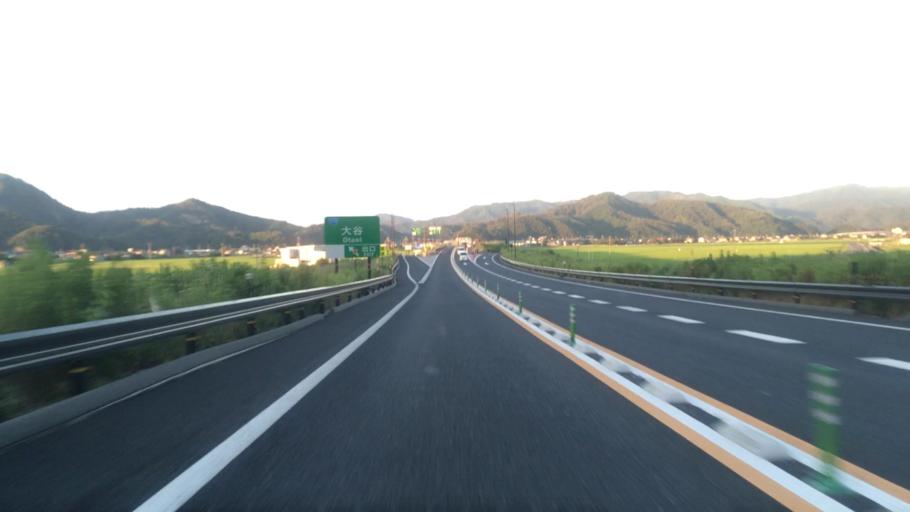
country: JP
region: Tottori
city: Tottori
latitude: 35.5687
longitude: 134.2950
